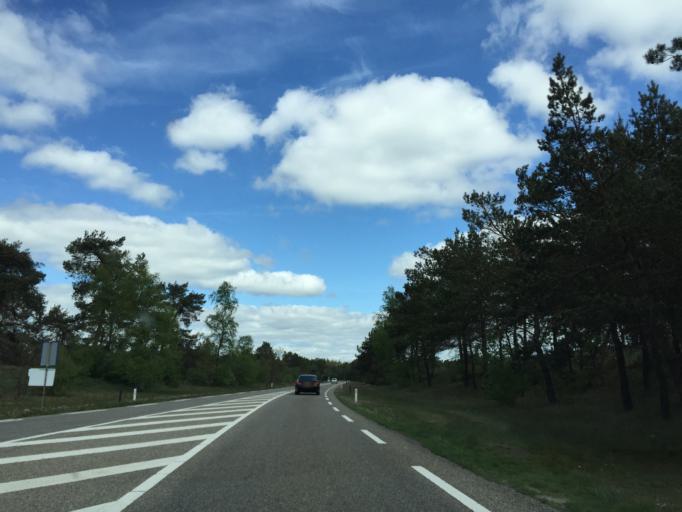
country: NL
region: Gelderland
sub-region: Gemeente Apeldoorn
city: Uddel
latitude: 52.2077
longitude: 5.7793
